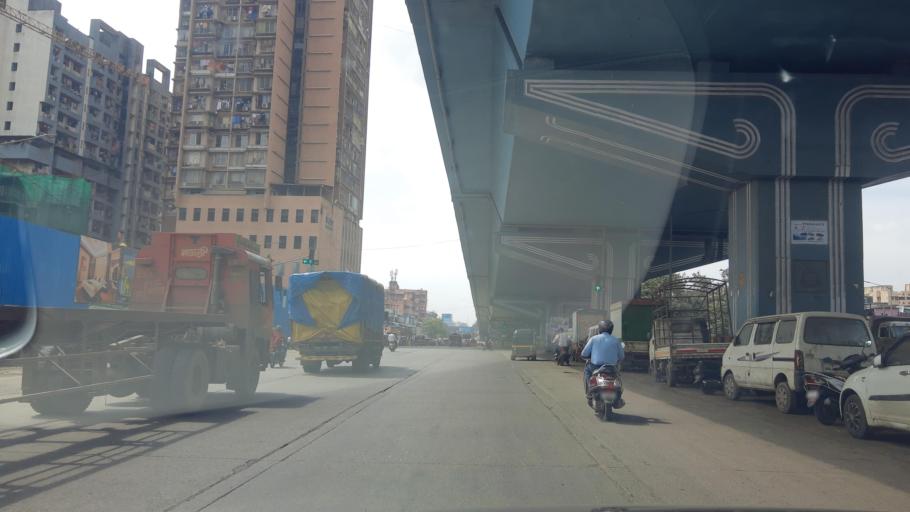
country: IN
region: Maharashtra
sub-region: Mumbai Suburban
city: Mumbai
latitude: 19.0617
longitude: 72.9189
